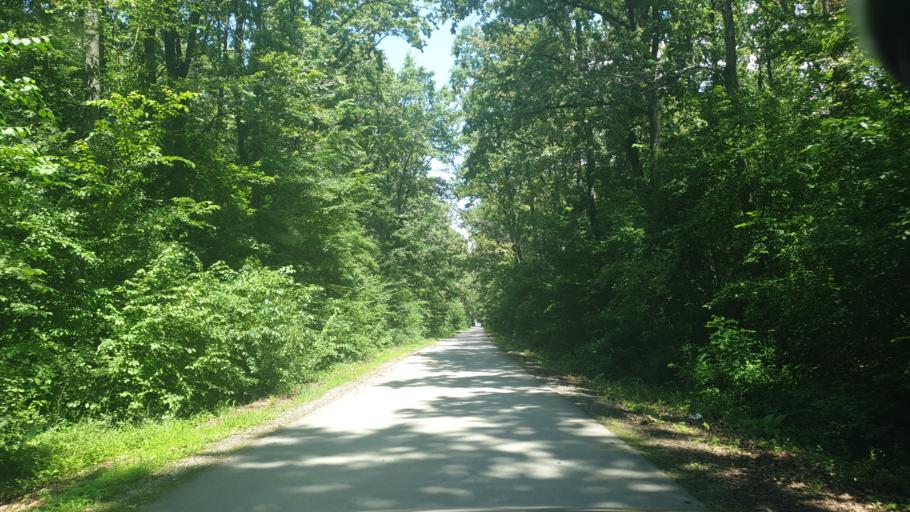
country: RS
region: Autonomna Pokrajina Vojvodina
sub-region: Sremski Okrug
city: Sid
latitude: 45.0395
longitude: 19.1383
